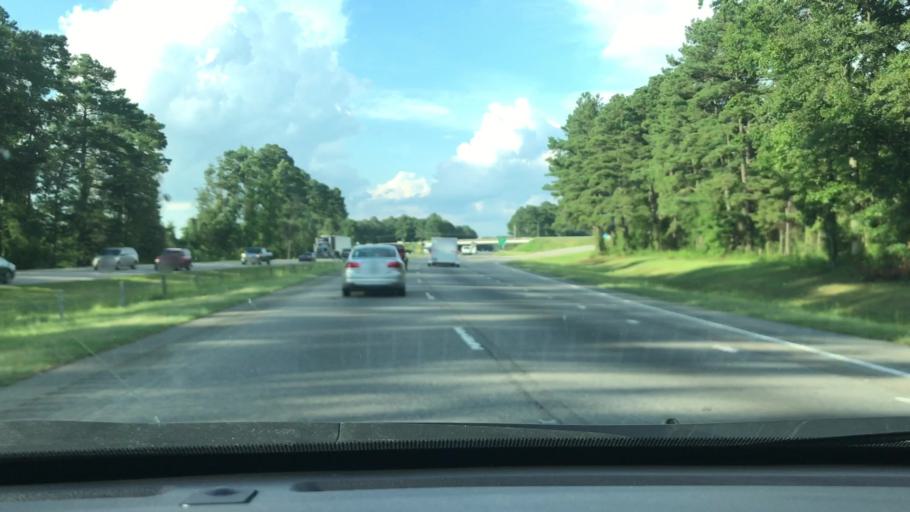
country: US
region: North Carolina
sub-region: Robeson County
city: Saint Pauls
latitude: 34.8302
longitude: -78.9812
